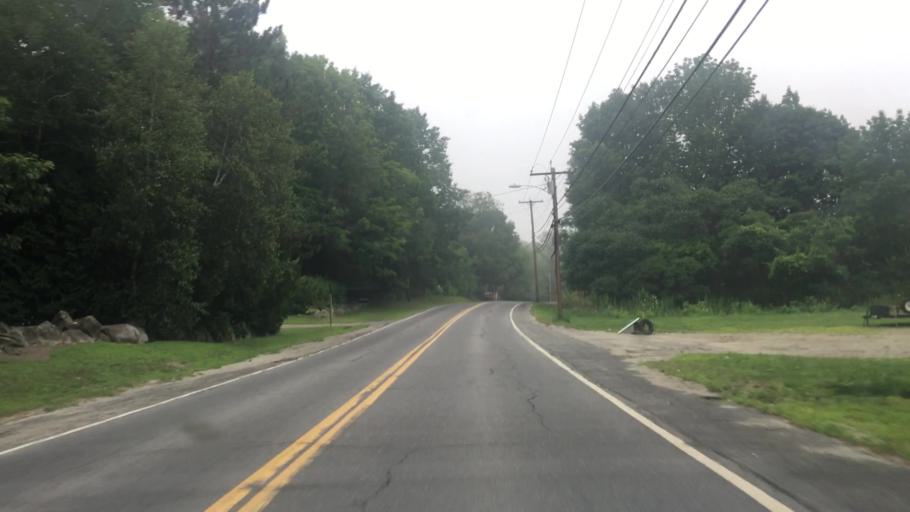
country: US
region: Maine
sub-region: Kennebec County
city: Oakland
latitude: 44.5351
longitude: -69.7230
